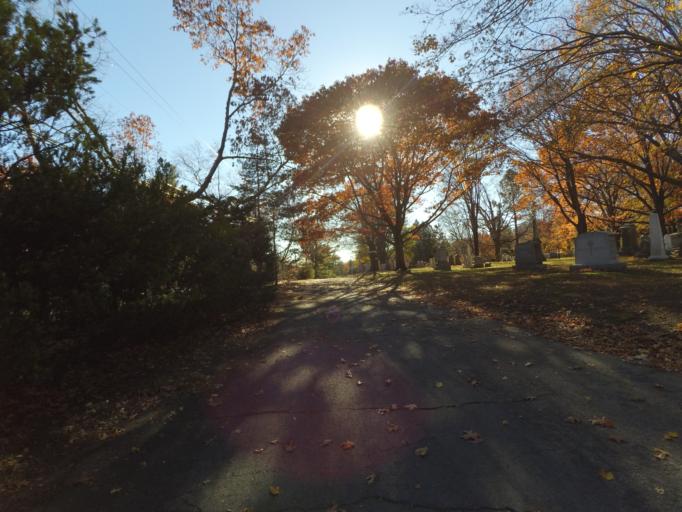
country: US
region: Massachusetts
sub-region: Middlesex County
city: Cambridge
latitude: 42.3725
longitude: -71.1401
